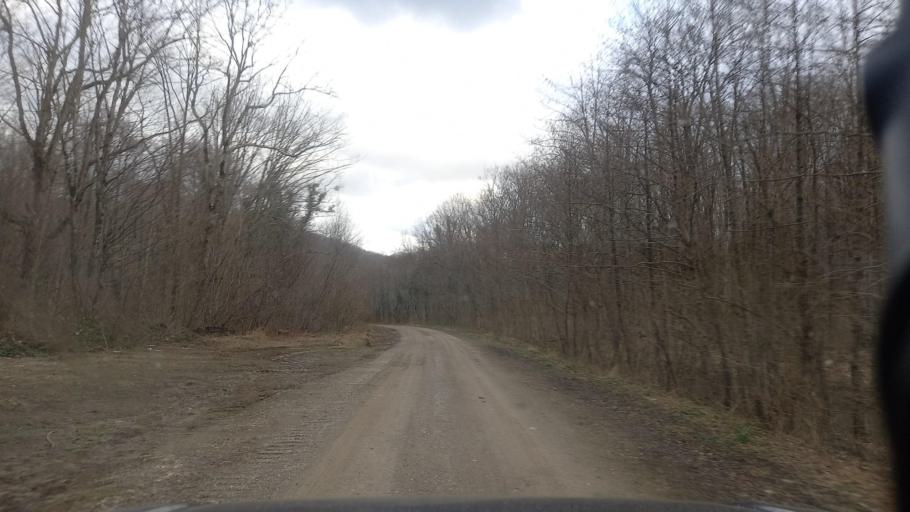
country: RU
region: Krasnodarskiy
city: Dzhubga
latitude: 44.4855
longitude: 38.7766
